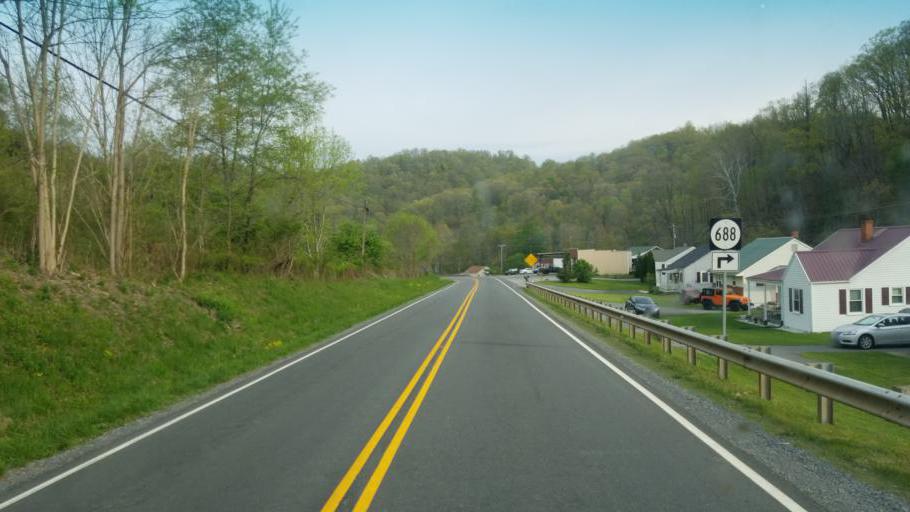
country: US
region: Virginia
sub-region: Smyth County
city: Marion
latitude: 36.8216
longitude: -81.4725
